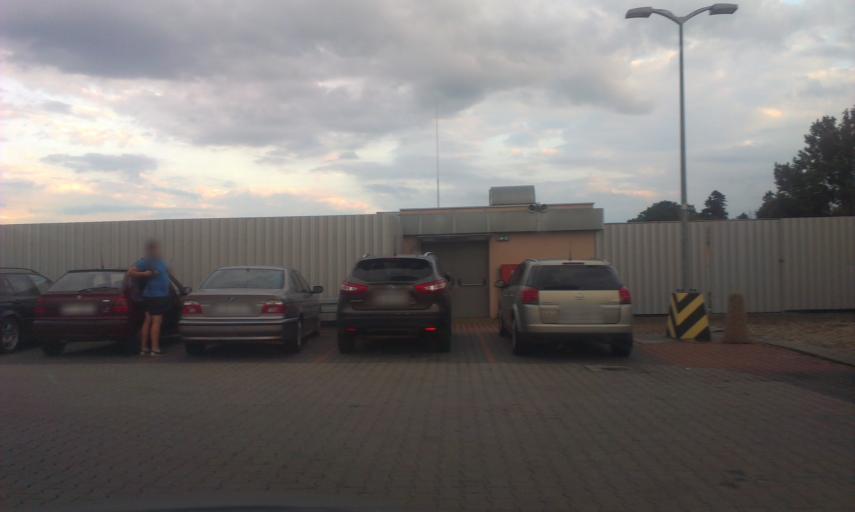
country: PL
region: West Pomeranian Voivodeship
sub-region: Koszalin
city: Koszalin
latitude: 54.1770
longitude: 16.2014
